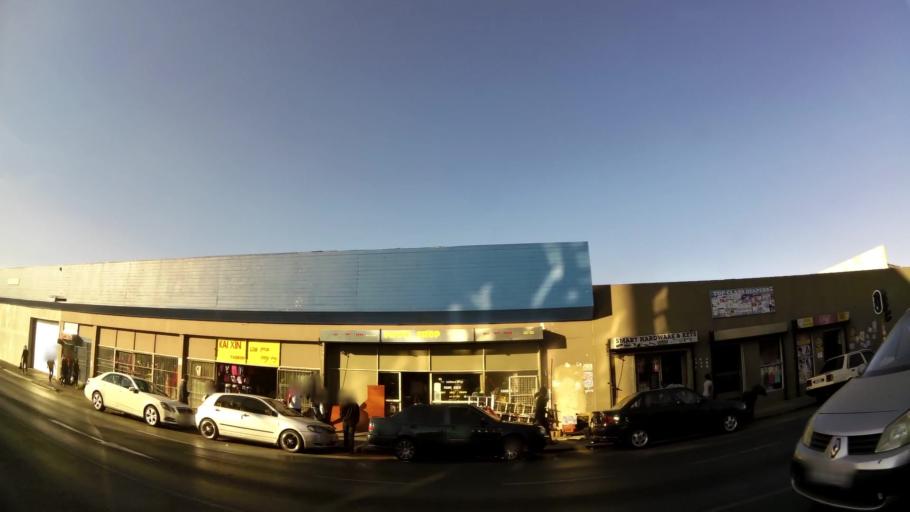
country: ZA
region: Gauteng
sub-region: City of Johannesburg Metropolitan Municipality
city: Roodepoort
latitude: -26.1615
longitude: 27.8699
